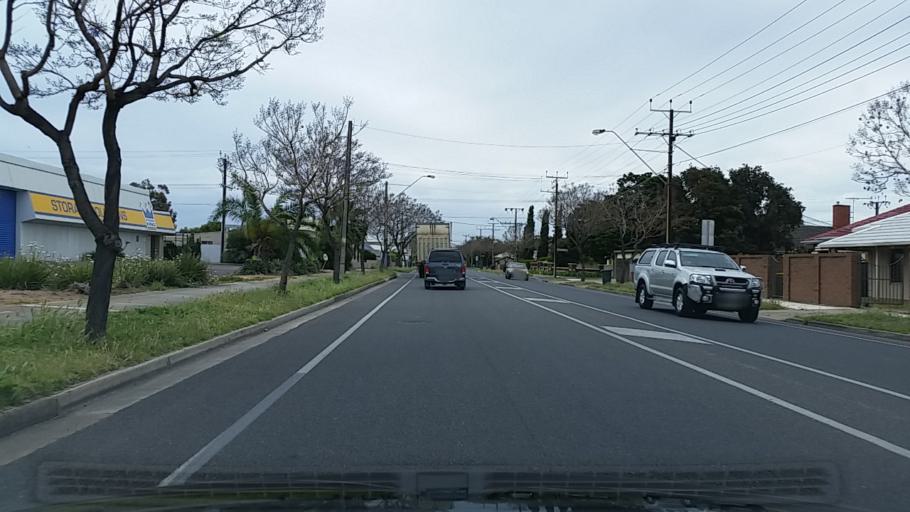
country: AU
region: South Australia
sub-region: Charles Sturt
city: Allenby Gardens
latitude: -34.8974
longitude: 138.5515
